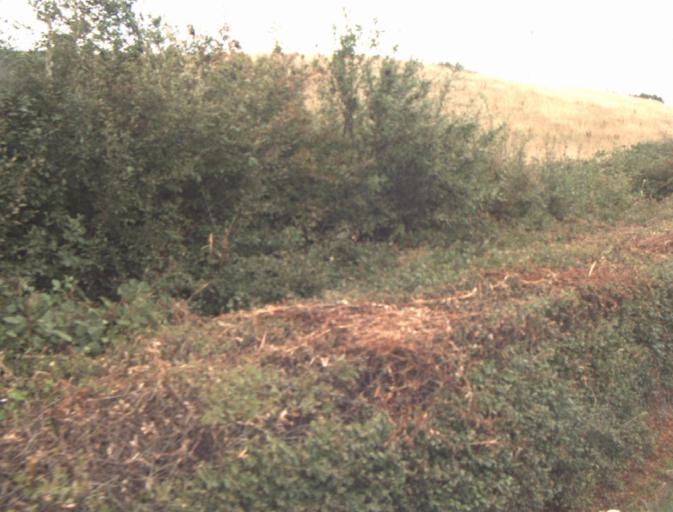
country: AU
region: Tasmania
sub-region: Northern Midlands
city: Evandale
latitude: -41.5236
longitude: 147.2476
